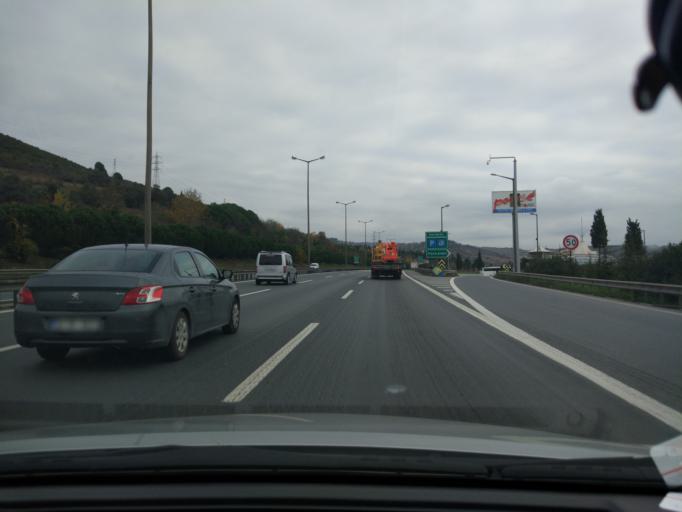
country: TR
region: Kocaeli
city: Izmit
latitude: 40.7732
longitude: 29.8713
